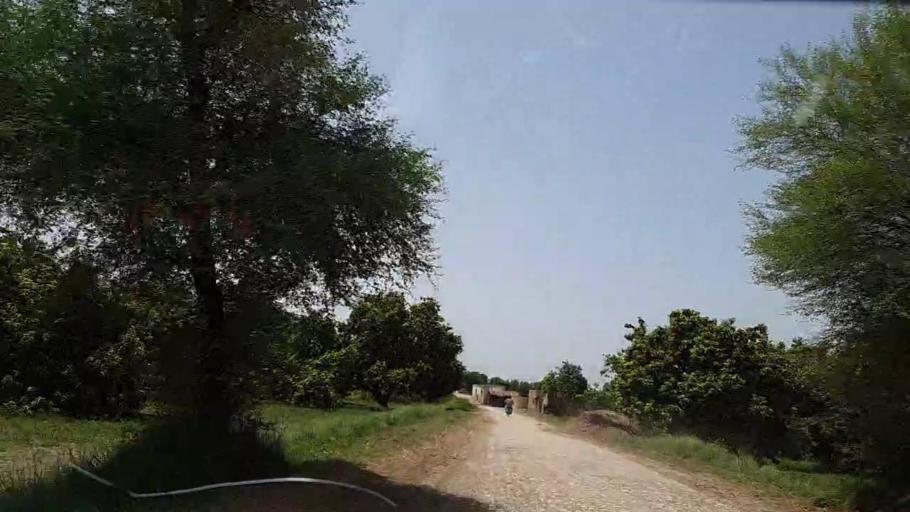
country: PK
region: Sindh
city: Tharu Shah
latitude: 26.9640
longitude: 68.0401
